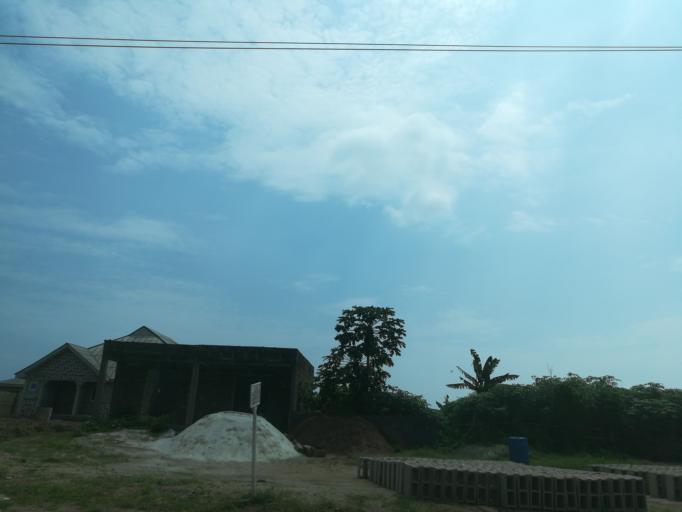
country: NG
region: Lagos
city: Ikorodu
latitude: 6.5964
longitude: 3.6324
